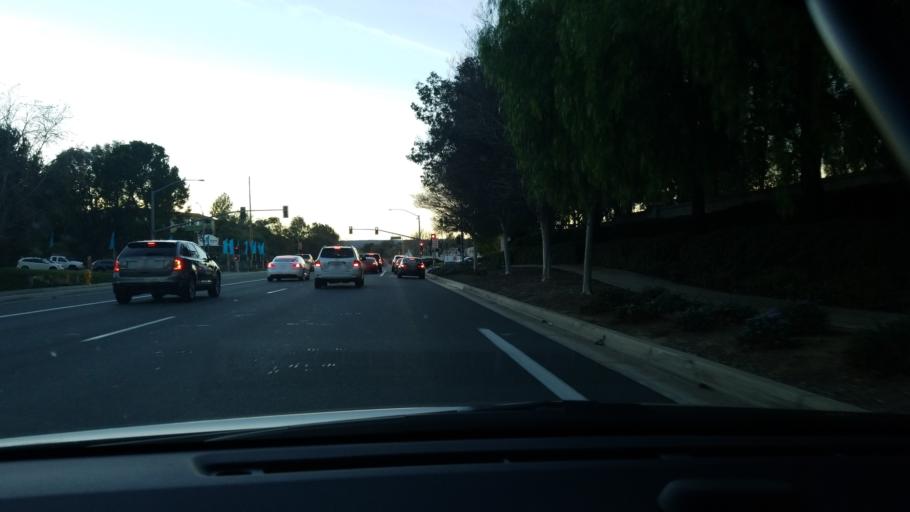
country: US
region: California
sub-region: Riverside County
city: Temecula
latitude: 33.5079
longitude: -117.1235
